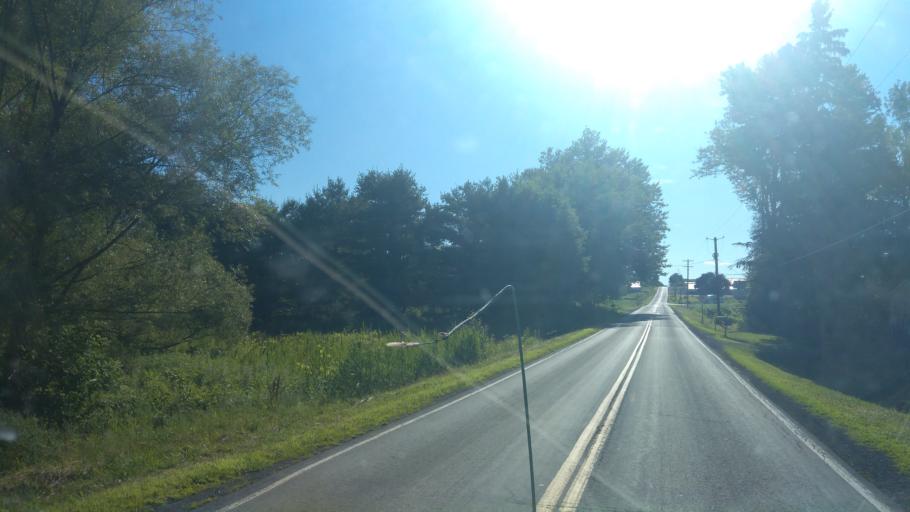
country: US
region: New York
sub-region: Wayne County
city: Lyons
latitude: 42.9950
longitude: -76.9243
